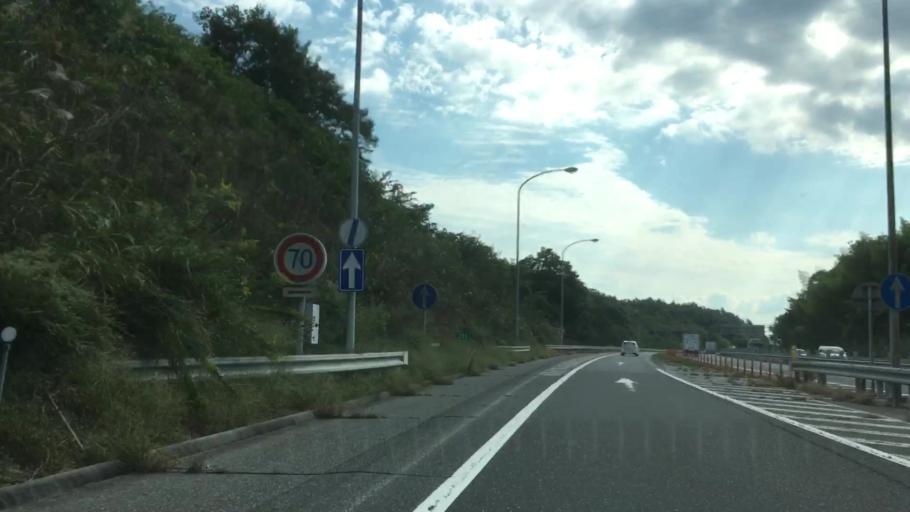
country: JP
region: Hiroshima
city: Miyajima
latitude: 34.3302
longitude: 132.2940
